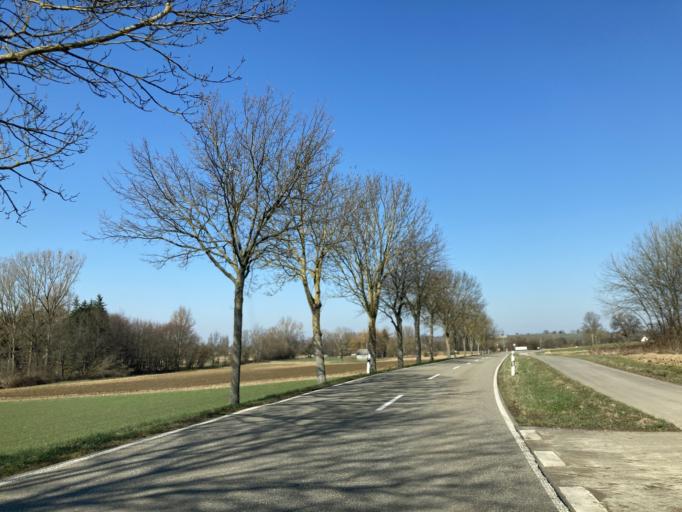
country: DE
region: Baden-Wuerttemberg
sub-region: Freiburg Region
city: Buggingen
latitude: 47.8291
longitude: 7.6519
